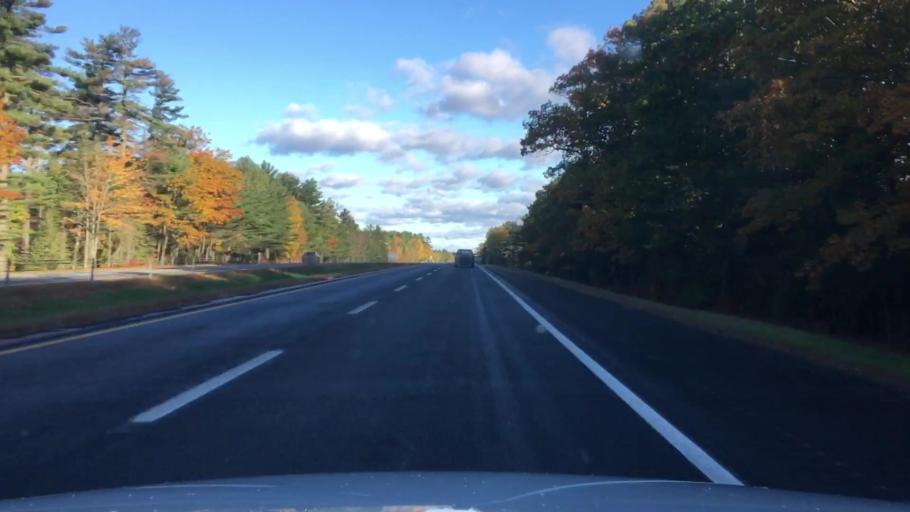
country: US
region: Maine
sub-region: Penobscot County
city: Orono
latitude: 44.9128
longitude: -68.6968
